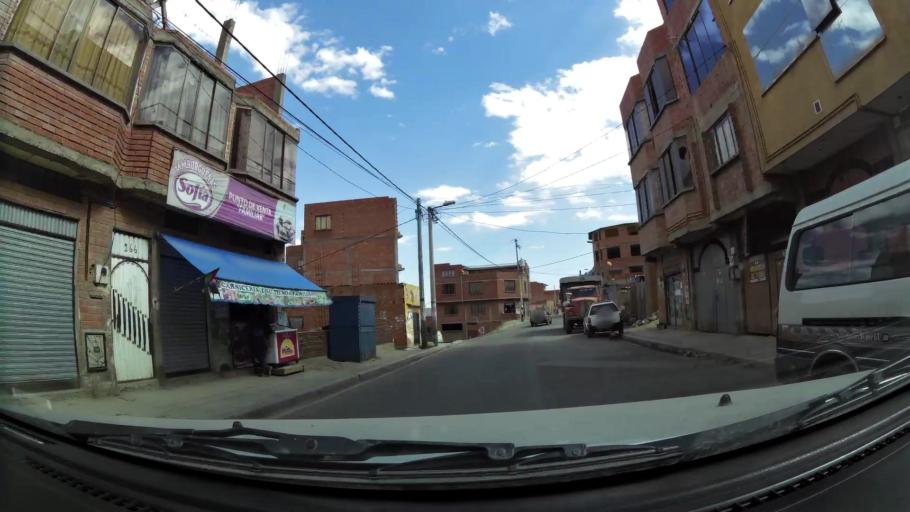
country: BO
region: La Paz
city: La Paz
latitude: -16.4590
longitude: -68.1032
